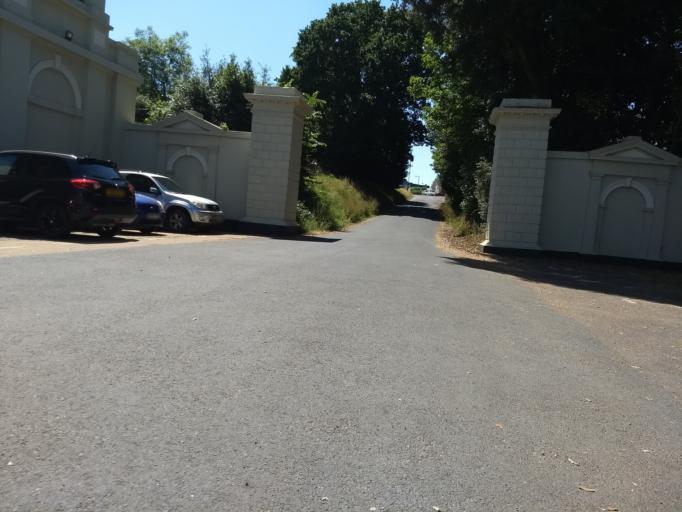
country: GB
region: England
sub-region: Isle of Wight
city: Cowes
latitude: 50.7636
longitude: -1.3036
